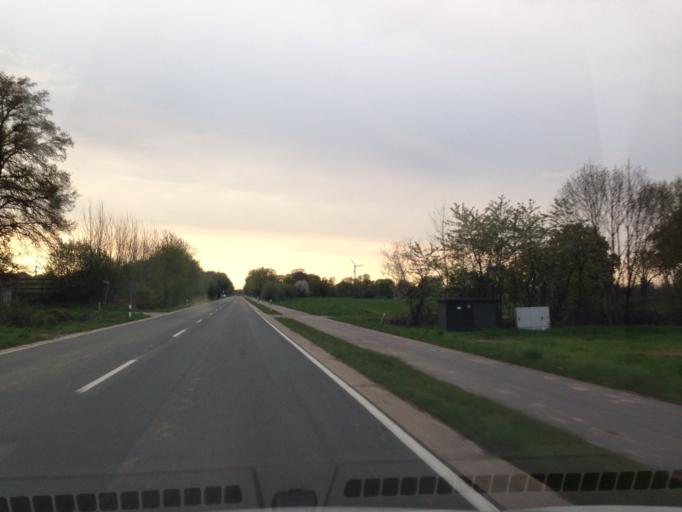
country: DE
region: North Rhine-Westphalia
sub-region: Regierungsbezirk Munster
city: Altenberge
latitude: 52.0644
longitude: 7.4475
